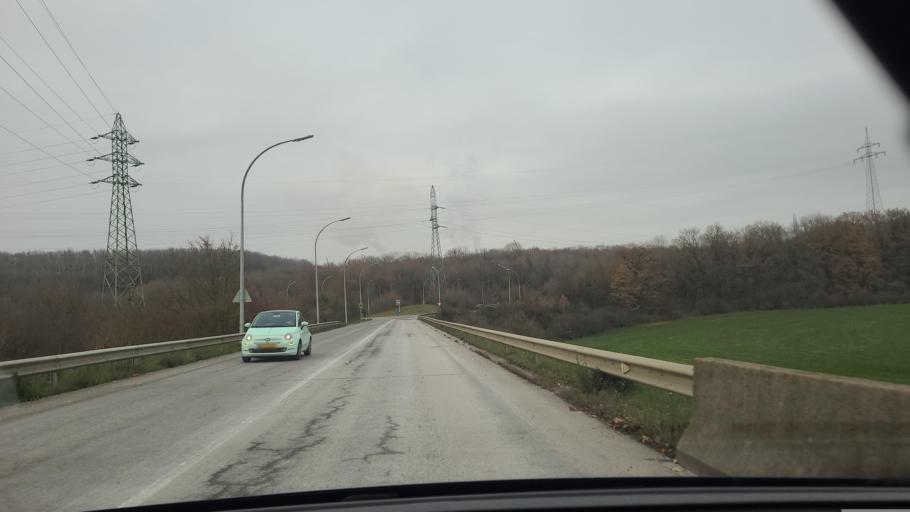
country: LU
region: Luxembourg
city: Belvaux
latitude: 49.5232
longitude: 5.9224
